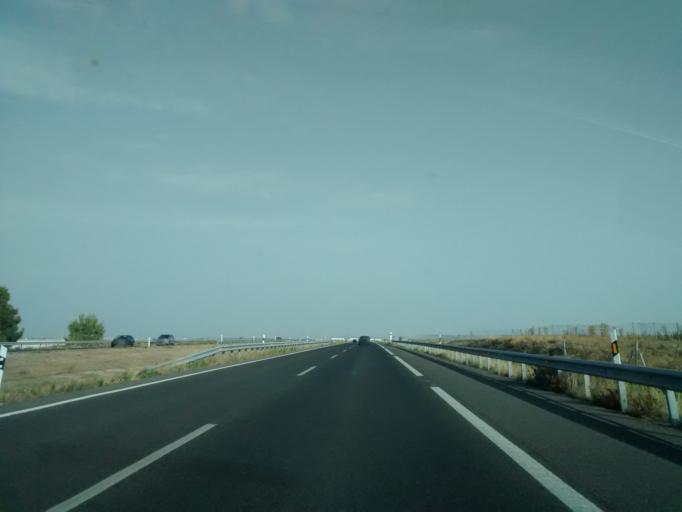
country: ES
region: Aragon
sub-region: Provincia de Zaragoza
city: Pedrola
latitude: 41.7770
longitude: -1.2343
